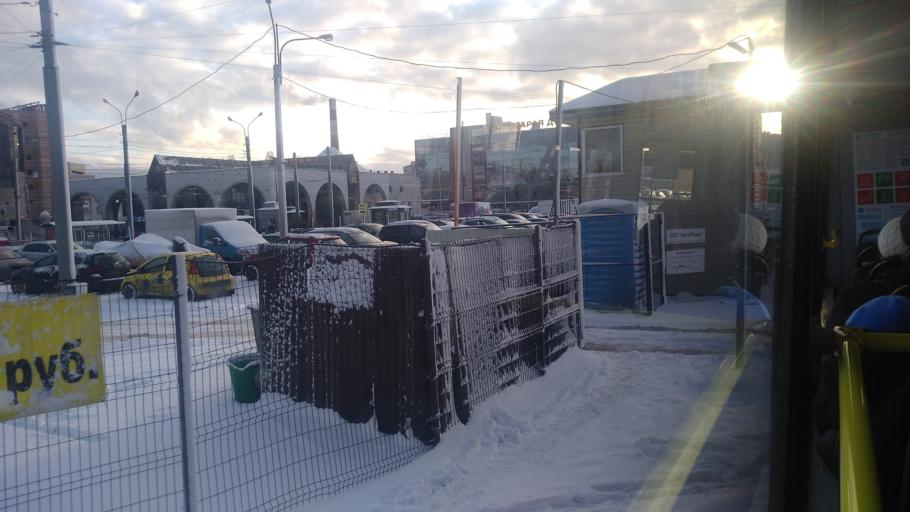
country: RU
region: St.-Petersburg
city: Staraya Derevnya
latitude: 59.9903
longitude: 30.2536
